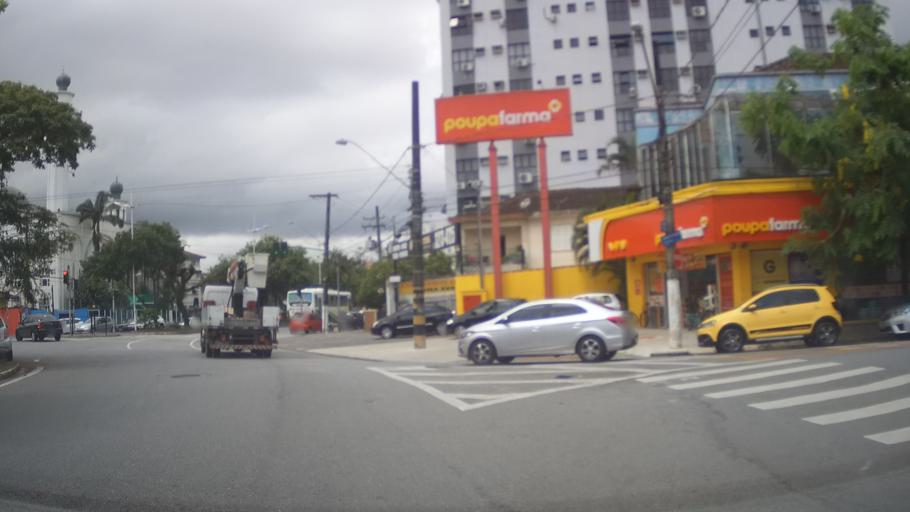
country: BR
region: Sao Paulo
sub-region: Santos
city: Santos
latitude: -23.9654
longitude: -46.3111
